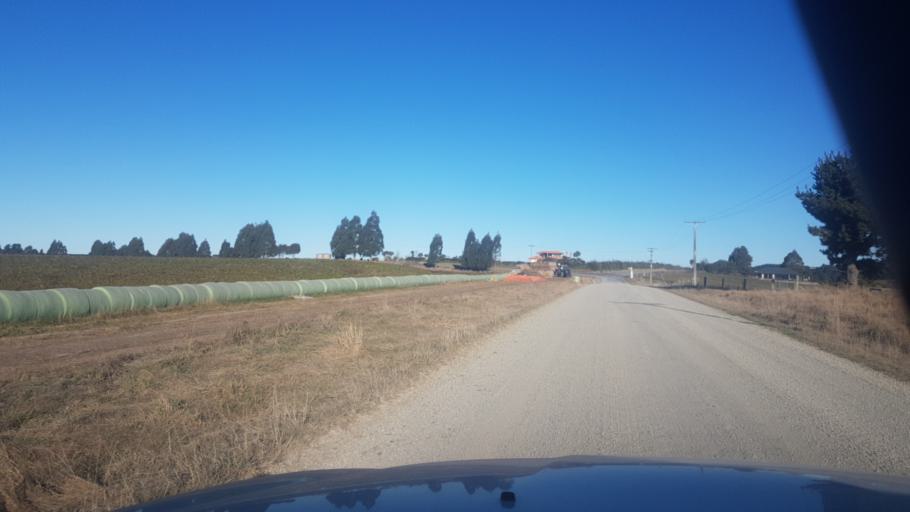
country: NZ
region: Canterbury
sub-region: Timaru District
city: Pleasant Point
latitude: -44.3579
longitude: 171.0694
